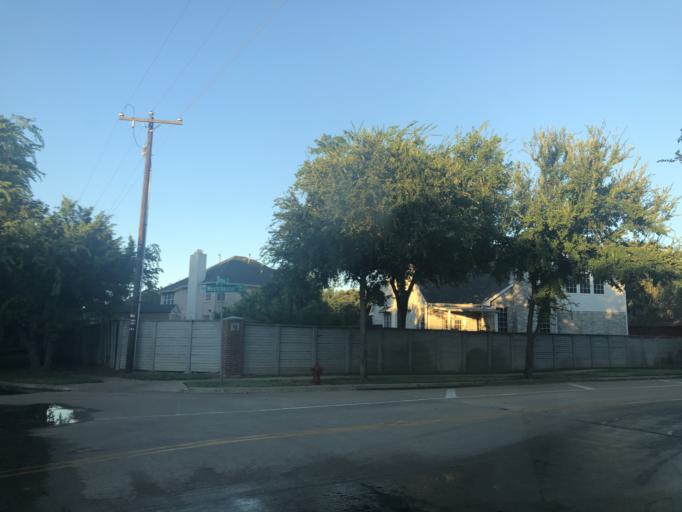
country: US
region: Texas
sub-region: Dallas County
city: Grand Prairie
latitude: 32.6718
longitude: -96.9983
